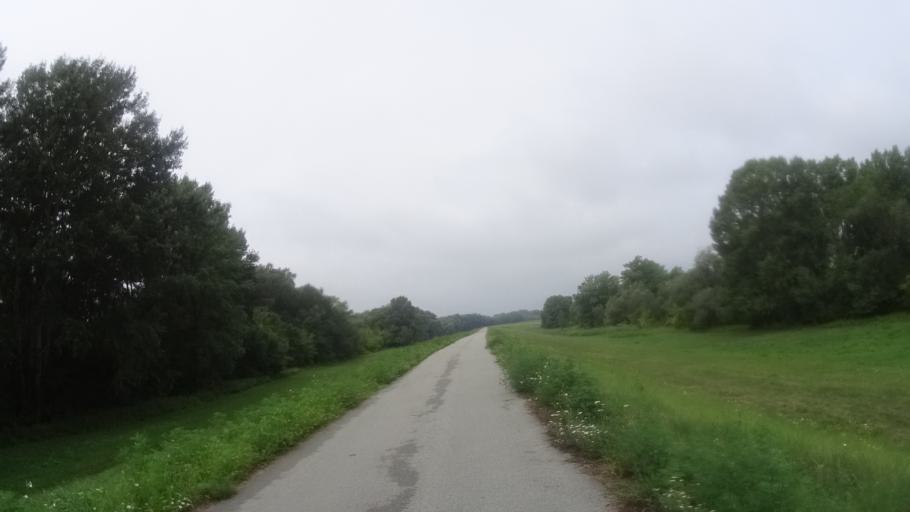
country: HU
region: Komarom-Esztergom
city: Almasfuzito
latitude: 47.7432
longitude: 18.1966
